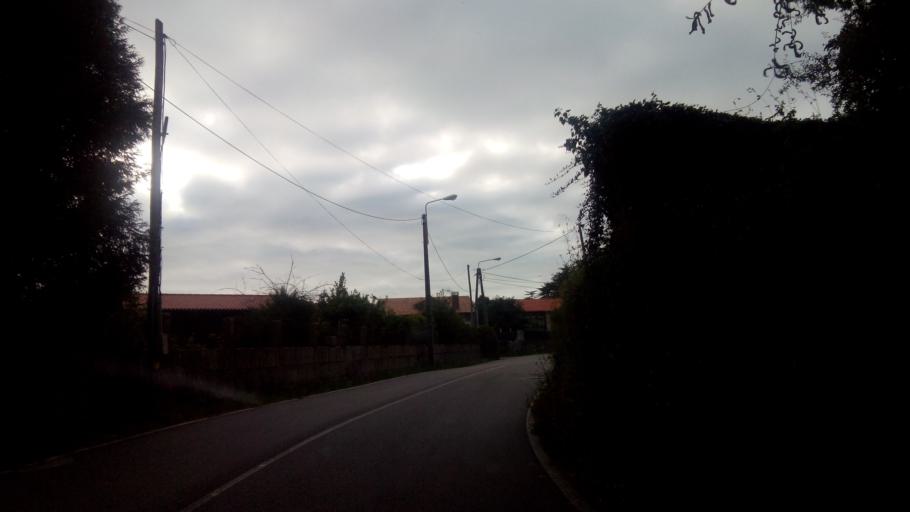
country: ES
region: Galicia
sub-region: Provincia de Pontevedra
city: Nigran
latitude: 42.1235
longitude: -8.8027
